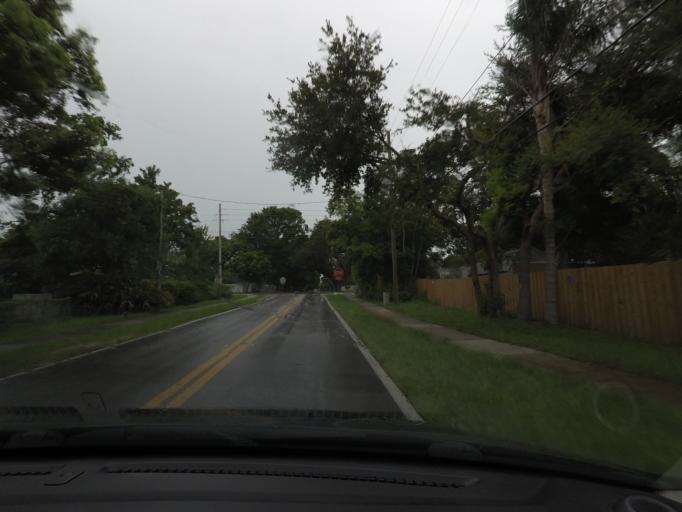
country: US
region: Florida
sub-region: Orange County
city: Edgewood
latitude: 28.4985
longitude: -81.3591
